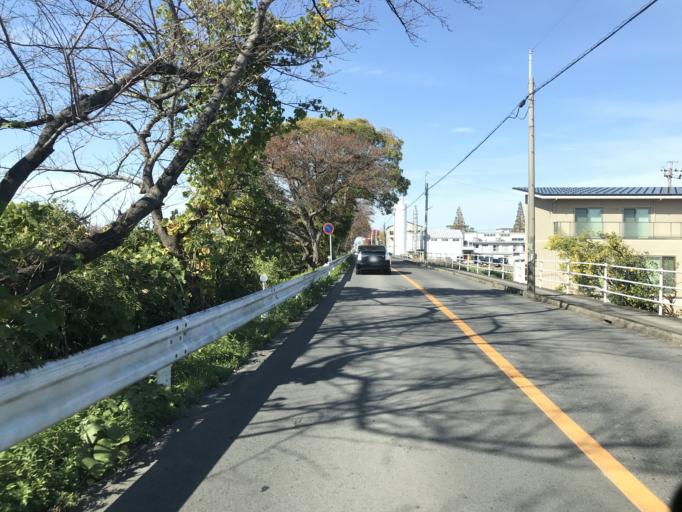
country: JP
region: Aichi
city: Iwakura
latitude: 35.2339
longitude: 136.8436
